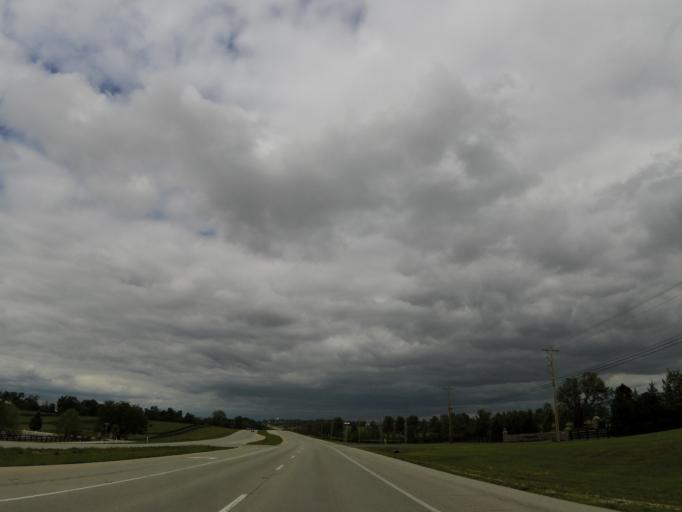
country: US
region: Kentucky
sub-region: Scott County
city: Georgetown
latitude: 38.1797
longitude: -84.5951
